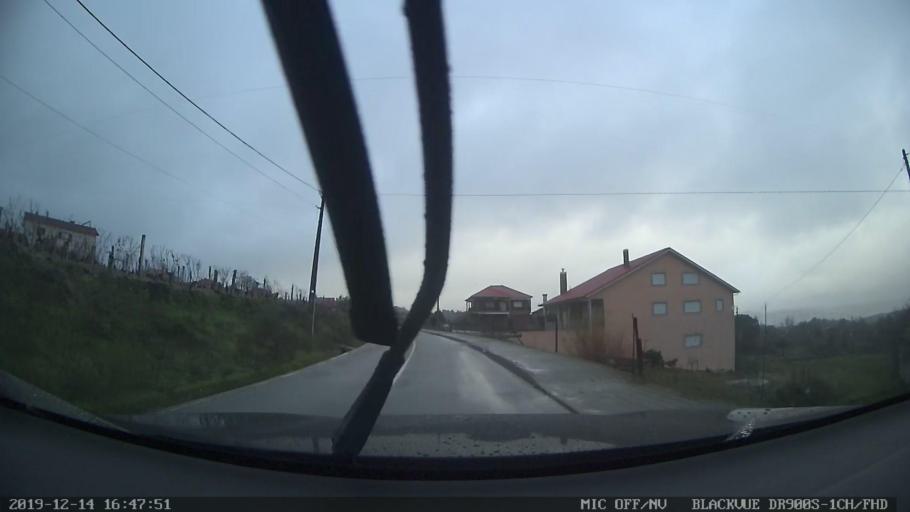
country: PT
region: Vila Real
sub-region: Murca
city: Murca
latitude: 41.4019
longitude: -7.5001
